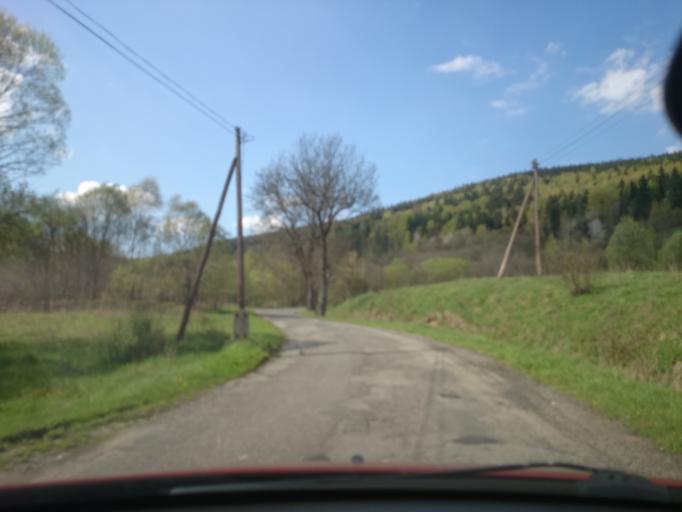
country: PL
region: Lower Silesian Voivodeship
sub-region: Powiat klodzki
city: Bystrzyca Klodzka
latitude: 50.2991
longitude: 16.5431
